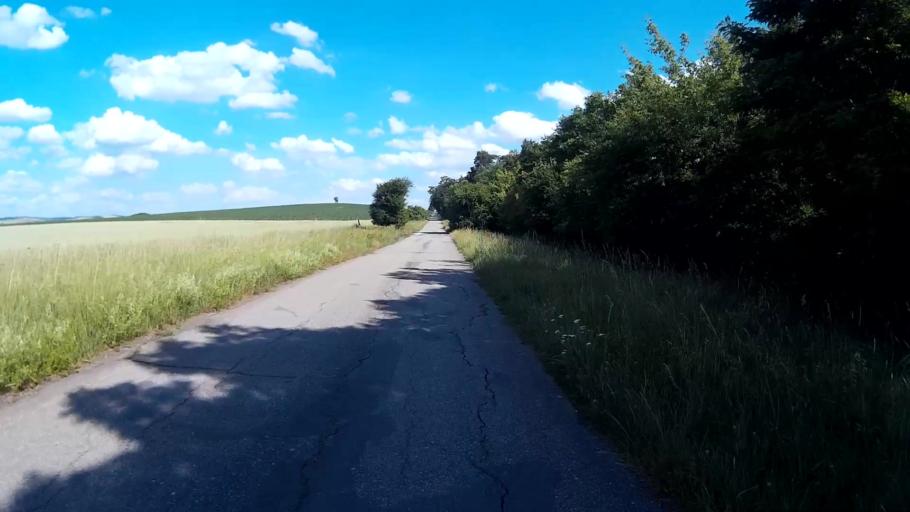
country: CZ
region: South Moravian
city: Moutnice
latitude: 49.0409
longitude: 16.7120
